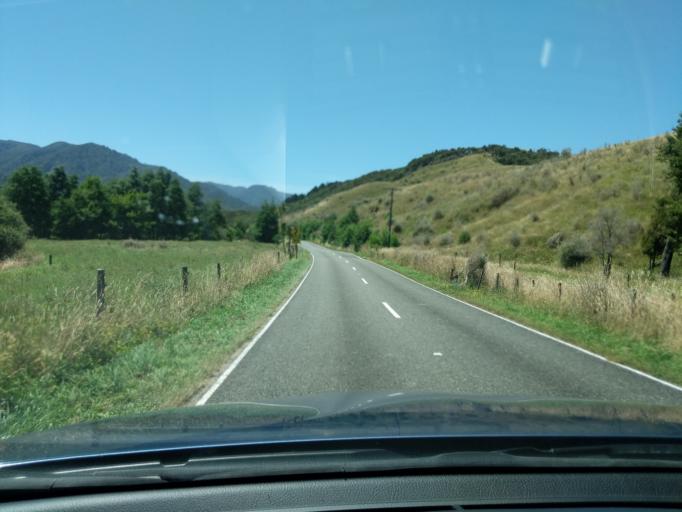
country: NZ
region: Tasman
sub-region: Tasman District
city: Takaka
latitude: -40.7365
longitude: 172.5811
